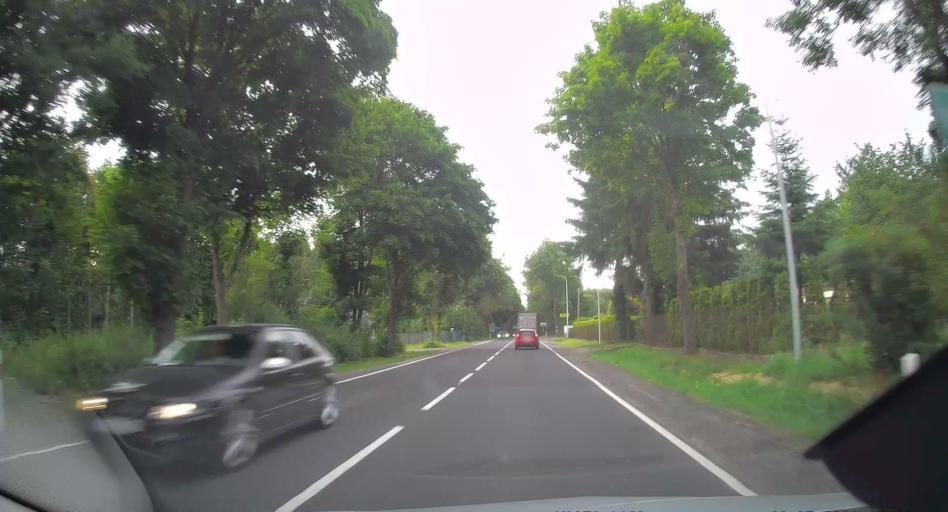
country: PL
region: Lodz Voivodeship
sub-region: Powiat radomszczanski
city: Gomunice
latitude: 51.1687
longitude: 19.4933
